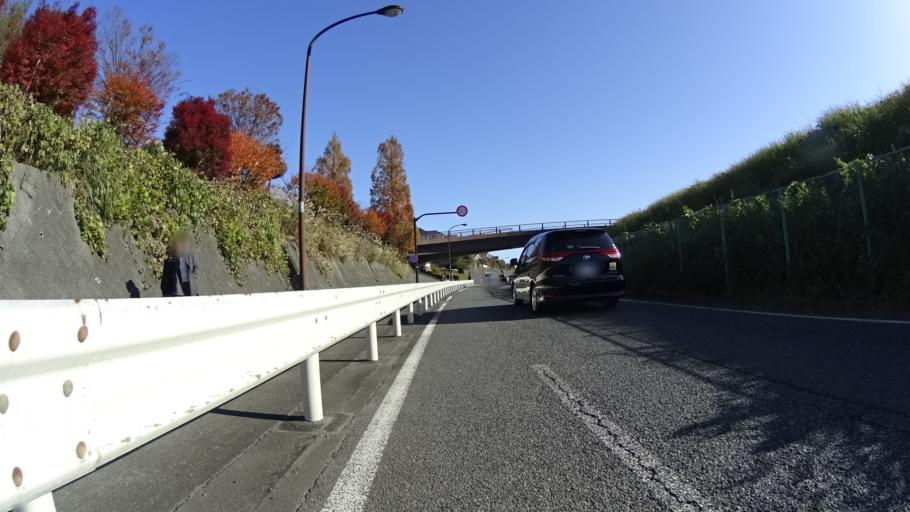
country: JP
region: Tokyo
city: Hino
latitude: 35.6125
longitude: 139.4169
